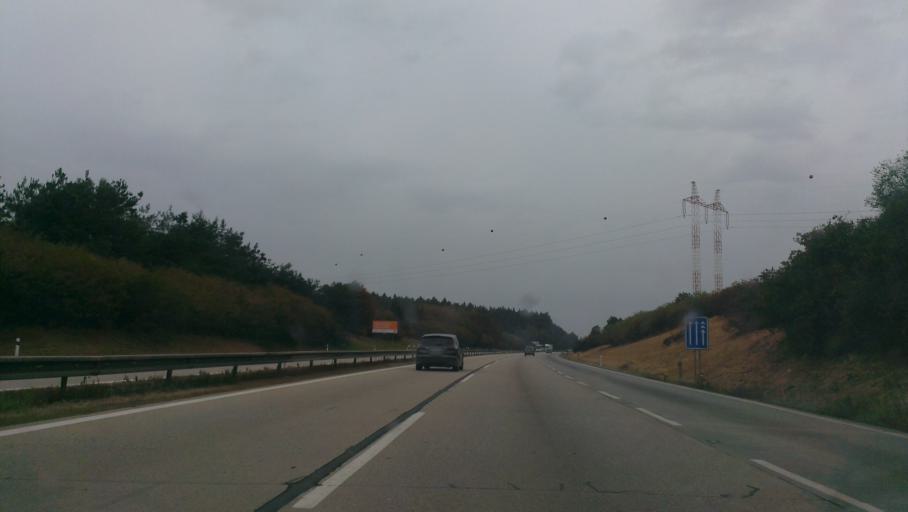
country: CZ
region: South Moravian
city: Ricany
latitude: 49.2255
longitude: 16.3888
